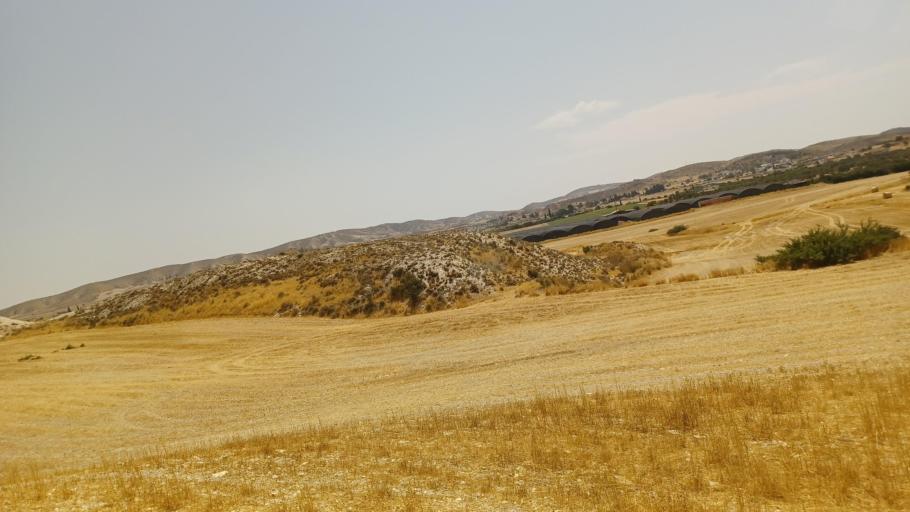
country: CY
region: Larnaka
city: Troulloi
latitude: 35.0318
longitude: 33.5983
